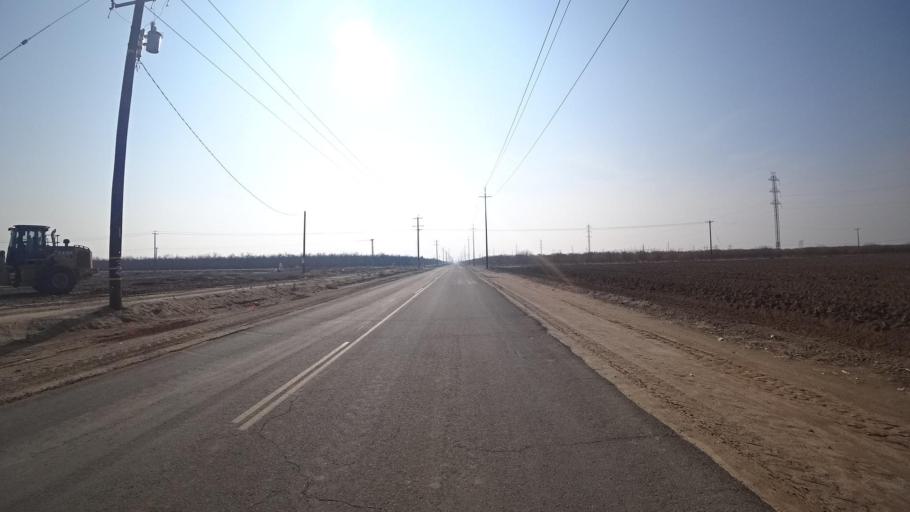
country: US
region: California
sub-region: Kern County
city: Buttonwillow
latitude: 35.4143
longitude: -119.4474
